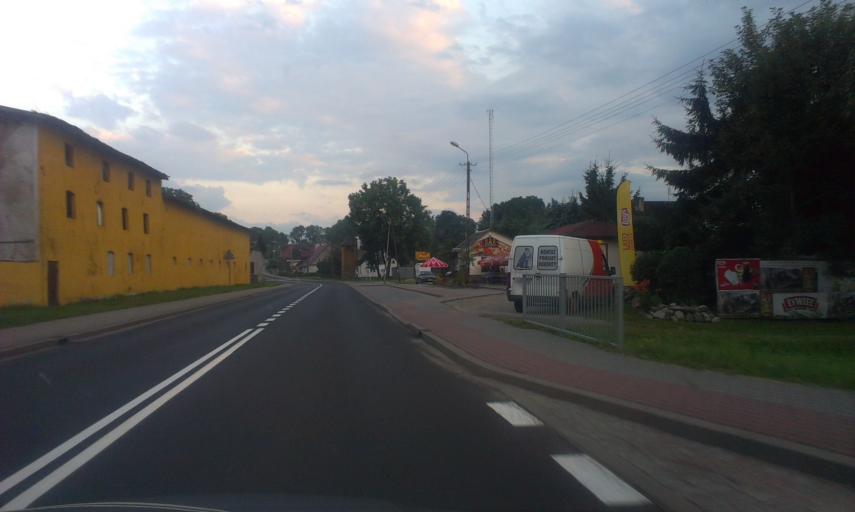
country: PL
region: West Pomeranian Voivodeship
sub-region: Powiat koszalinski
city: Bobolice
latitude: 54.0335
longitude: 16.4625
